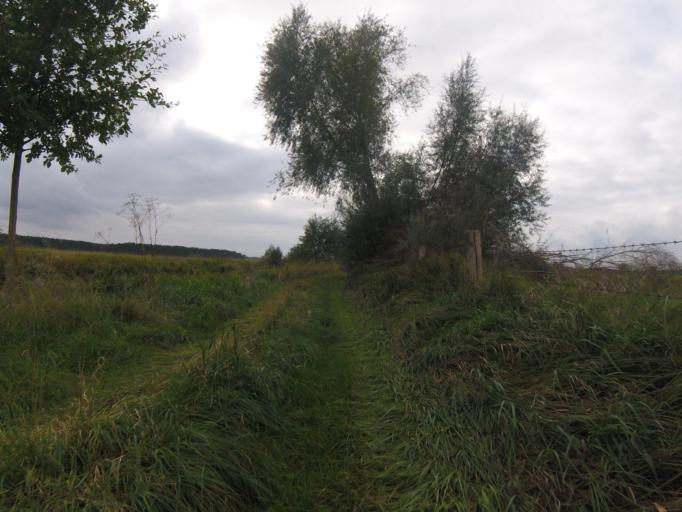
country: DE
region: Brandenburg
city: Mittenwalde
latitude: 52.2617
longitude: 13.5035
